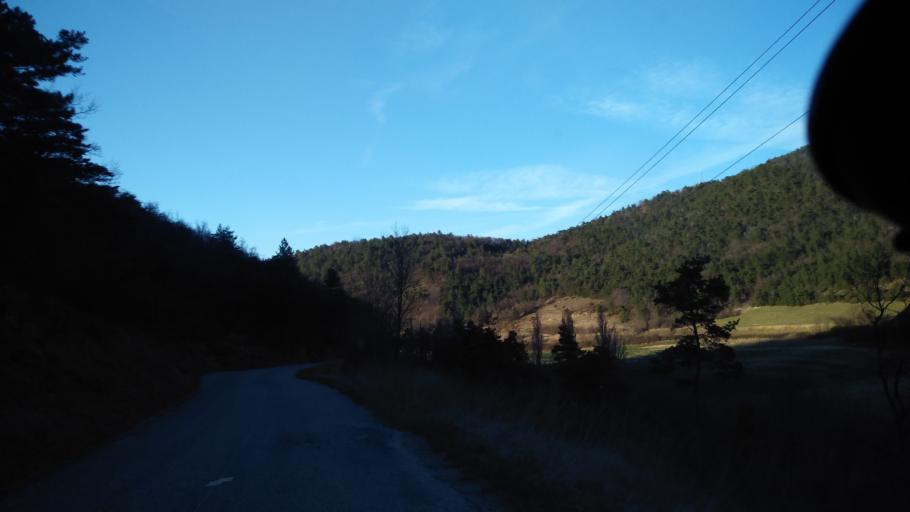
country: FR
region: Rhone-Alpes
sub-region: Departement de la Drome
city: Chabeuil
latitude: 44.8671
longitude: 5.0893
